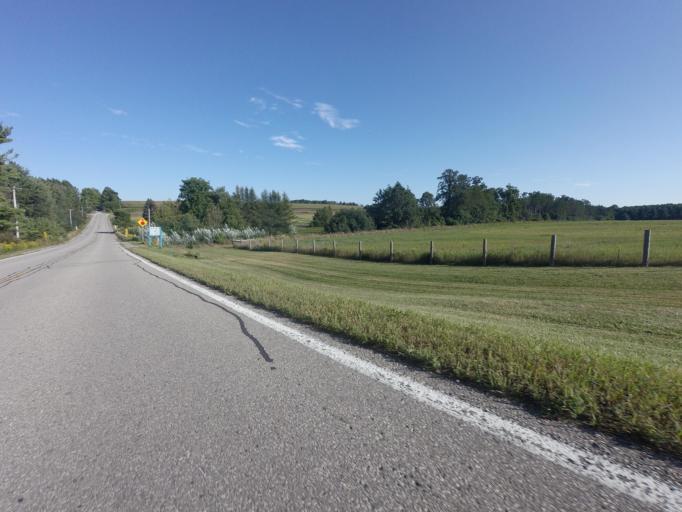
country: CA
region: Ontario
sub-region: Wellington County
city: Guelph
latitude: 43.6507
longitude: -80.4157
